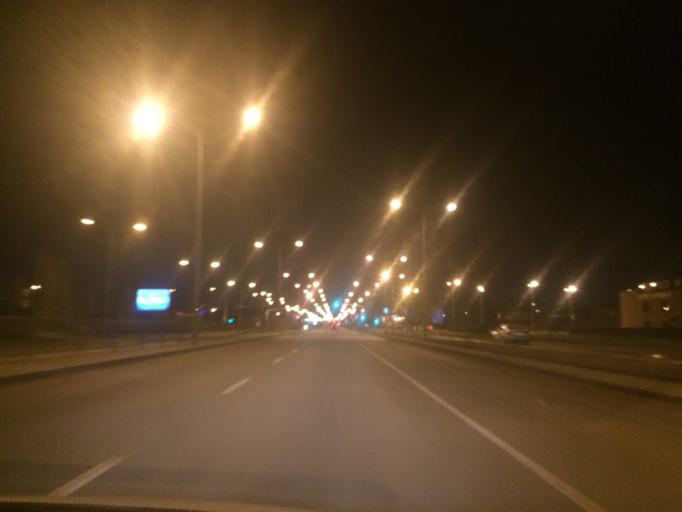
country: KZ
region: Astana Qalasy
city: Astana
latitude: 51.1477
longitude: 71.3942
